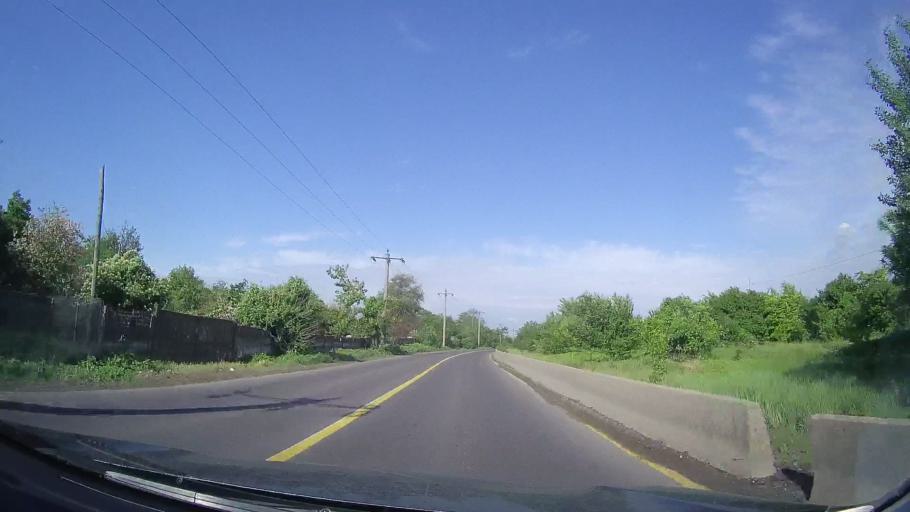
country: RO
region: Ilfov
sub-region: Comuna Vidra
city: Sintesti
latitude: 44.3354
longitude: 26.1338
